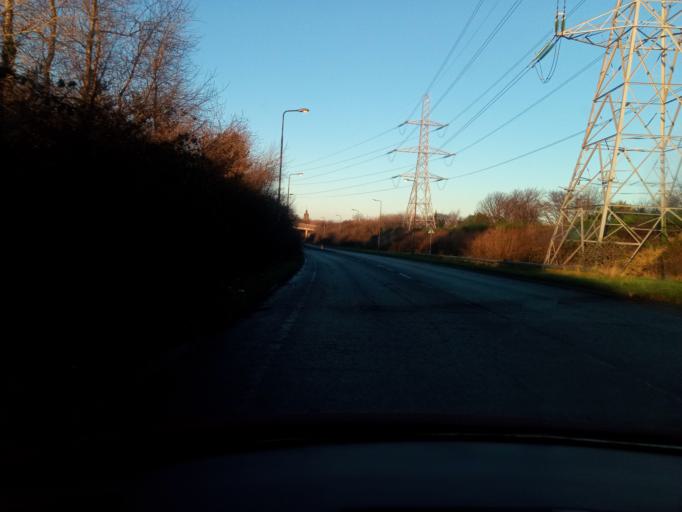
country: GB
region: Scotland
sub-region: West Lothian
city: Seafield
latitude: 55.9485
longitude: -3.1061
